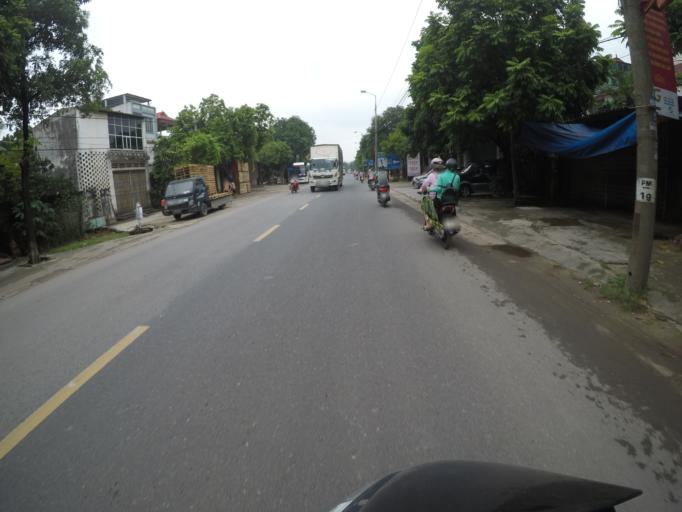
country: VN
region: Ha Noi
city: Soc Son
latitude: 21.2684
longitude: 105.8542
